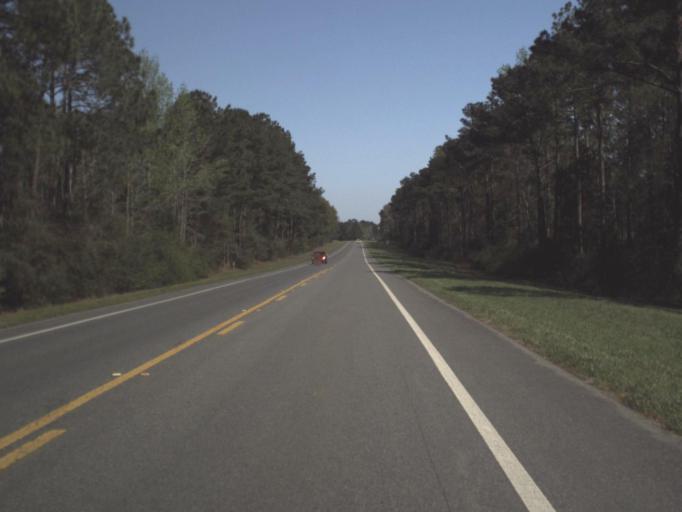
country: US
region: Florida
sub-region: Walton County
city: DeFuniak Springs
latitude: 30.7250
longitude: -85.9604
